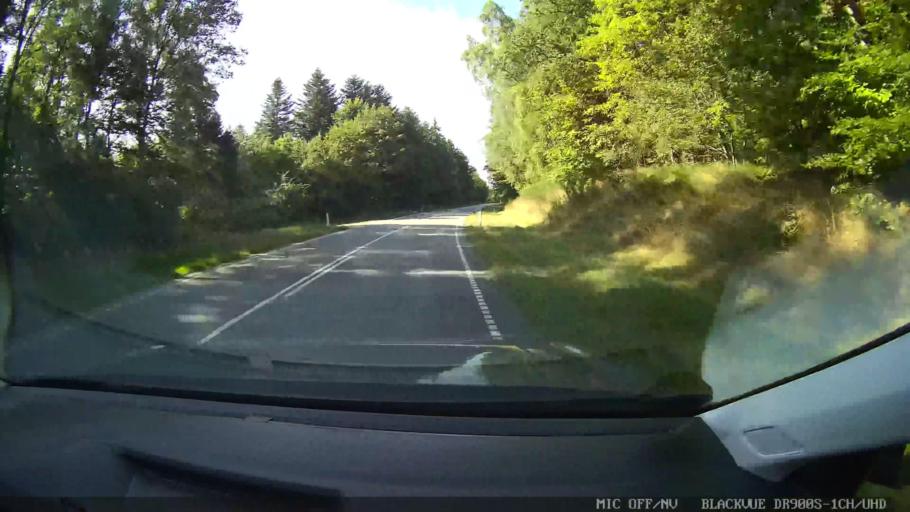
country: DK
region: North Denmark
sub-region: Mariagerfjord Kommune
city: Mariager
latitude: 56.6999
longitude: 10.0203
